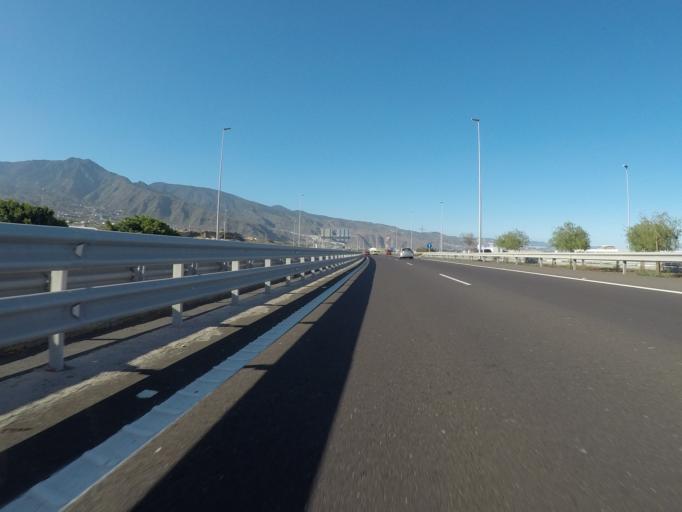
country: ES
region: Canary Islands
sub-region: Provincia de Santa Cruz de Tenerife
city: Candelaria
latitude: 28.3322
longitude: -16.3746
